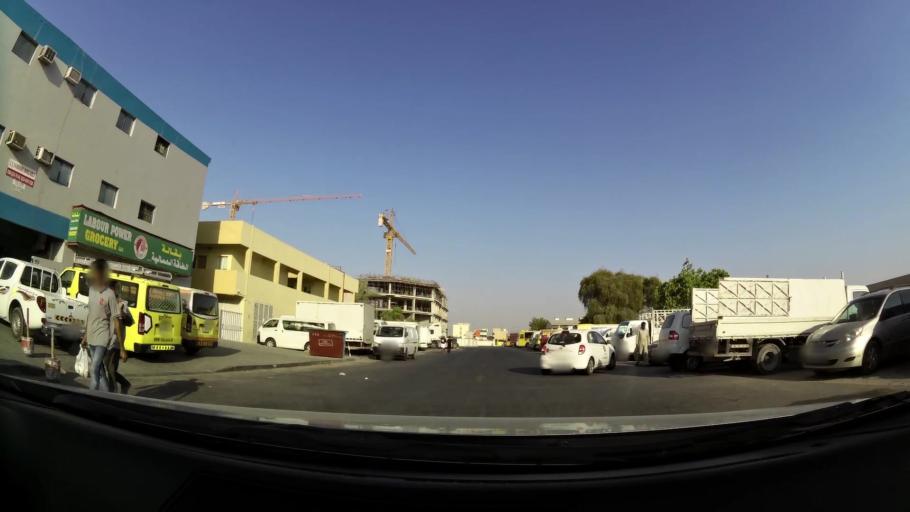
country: AE
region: Dubai
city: Dubai
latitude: 25.1304
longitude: 55.2364
